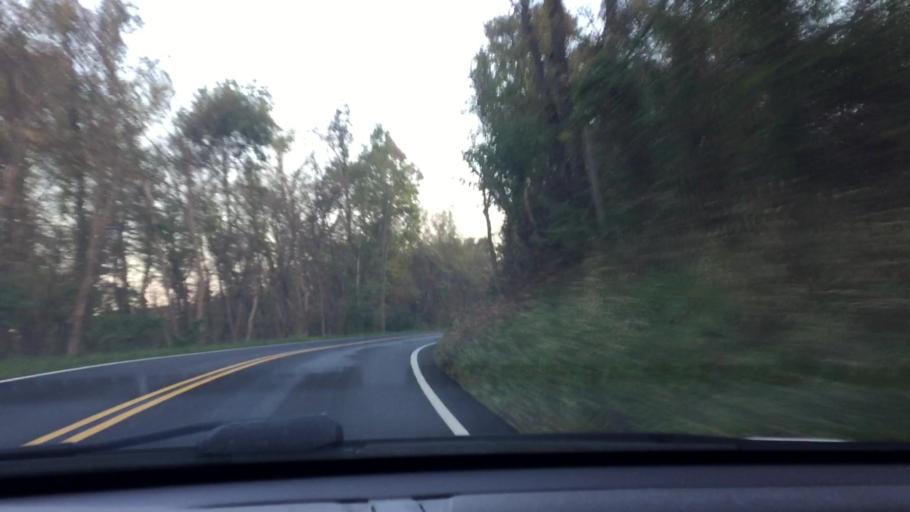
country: US
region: Pennsylvania
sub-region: Westmoreland County
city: Fellsburg
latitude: 40.1922
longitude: -79.8292
